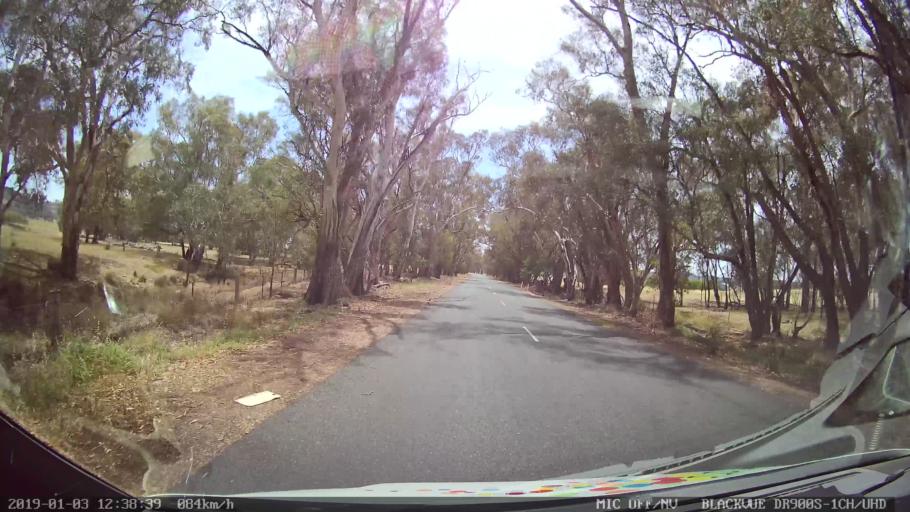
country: AU
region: New South Wales
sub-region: Weddin
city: Grenfell
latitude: -33.8317
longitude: 148.1982
